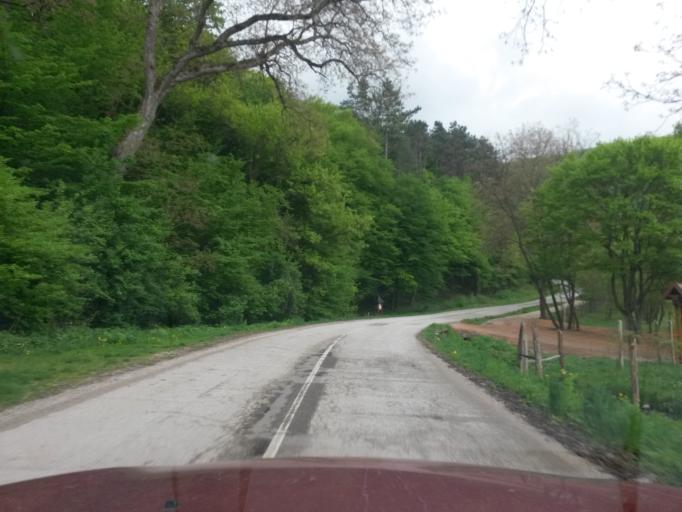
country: SK
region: Kosicky
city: Roznava
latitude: 48.5680
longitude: 20.4673
